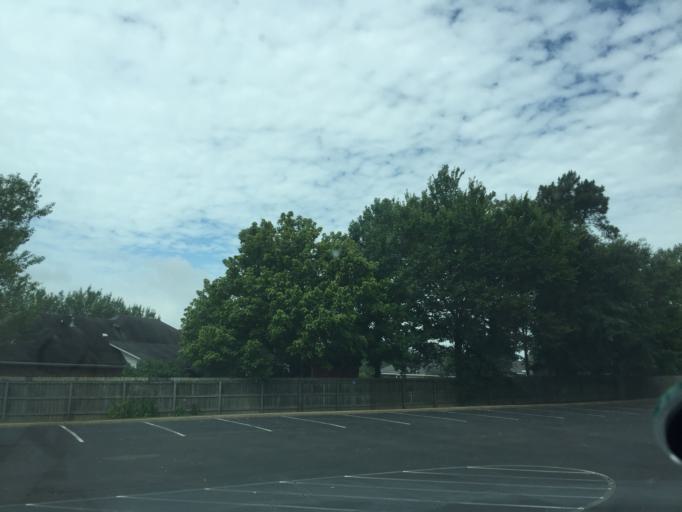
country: US
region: Mississippi
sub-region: Rankin County
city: Brandon
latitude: 32.2938
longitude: -89.9982
